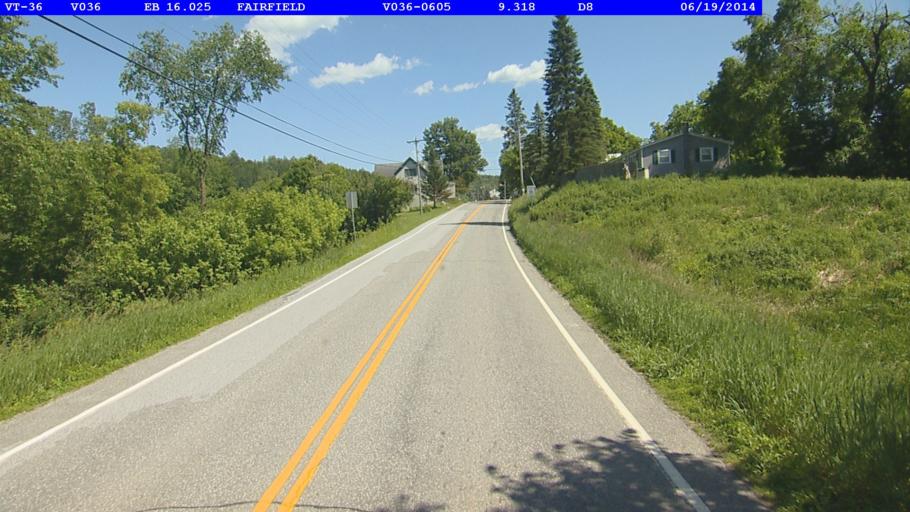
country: US
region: Vermont
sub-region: Franklin County
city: Enosburg Falls
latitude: 44.7862
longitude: -72.8610
